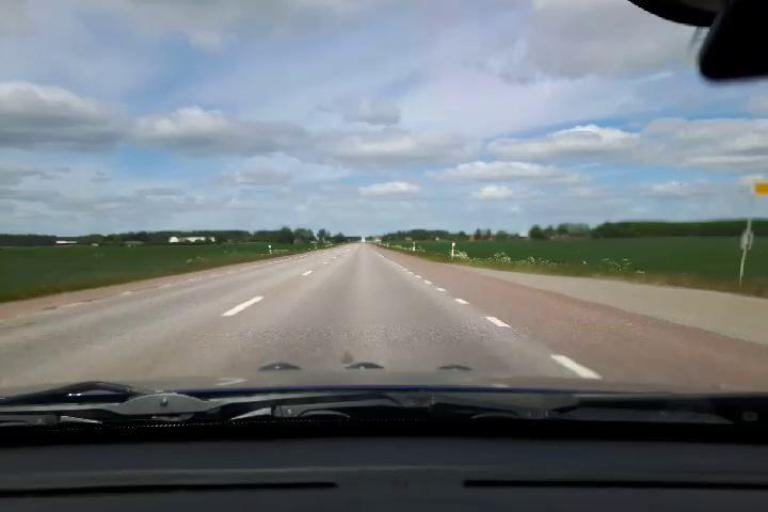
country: SE
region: Uppsala
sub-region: Uppsala Kommun
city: Gamla Uppsala
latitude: 59.9207
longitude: 17.6027
